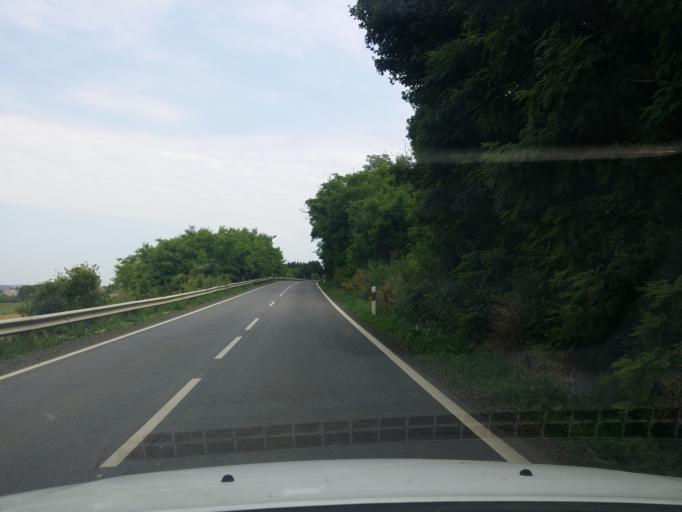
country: HU
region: Pest
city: Acsa
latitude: 47.7667
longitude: 19.3704
